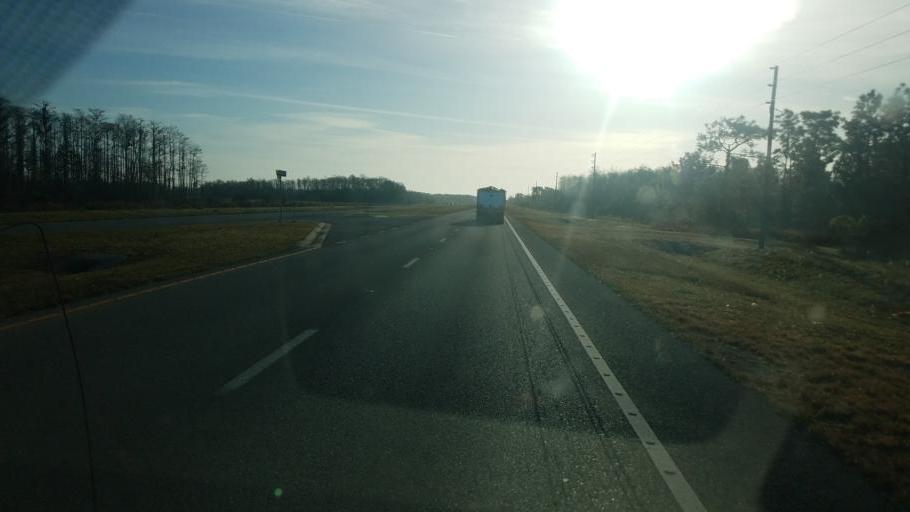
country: US
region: Florida
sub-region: Osceola County
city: Saint Cloud
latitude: 28.1420
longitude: -81.0572
